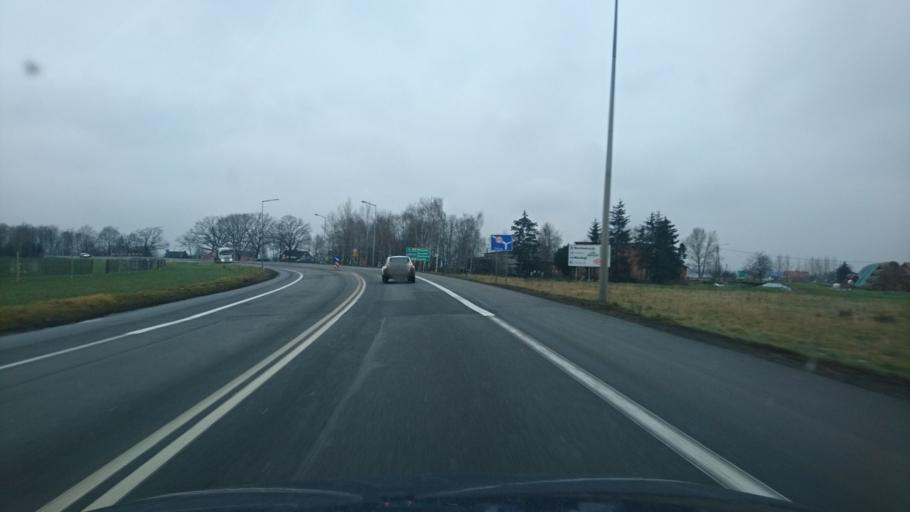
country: PL
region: Lodz Voivodeship
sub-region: Powiat wieruszowski
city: Walichnowy
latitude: 51.3063
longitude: 18.3805
